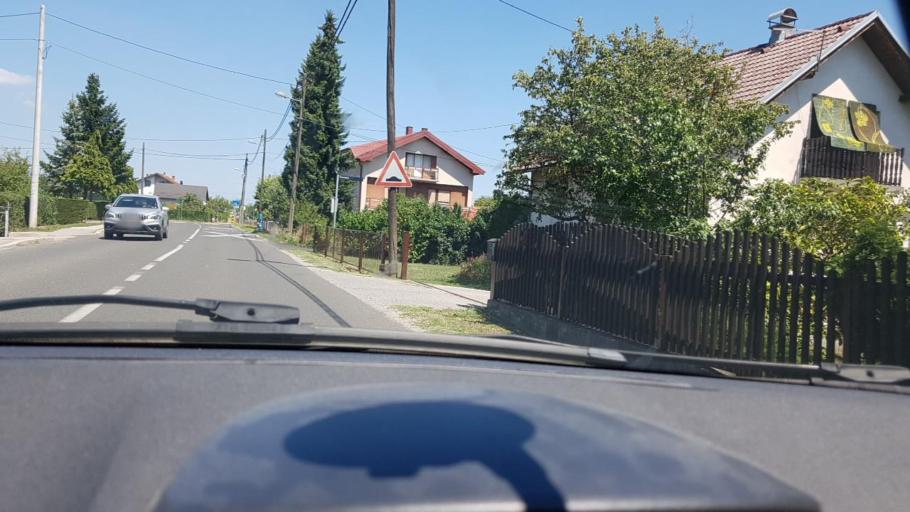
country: HR
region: Grad Zagreb
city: Brezovica
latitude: 45.7474
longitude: 15.8874
